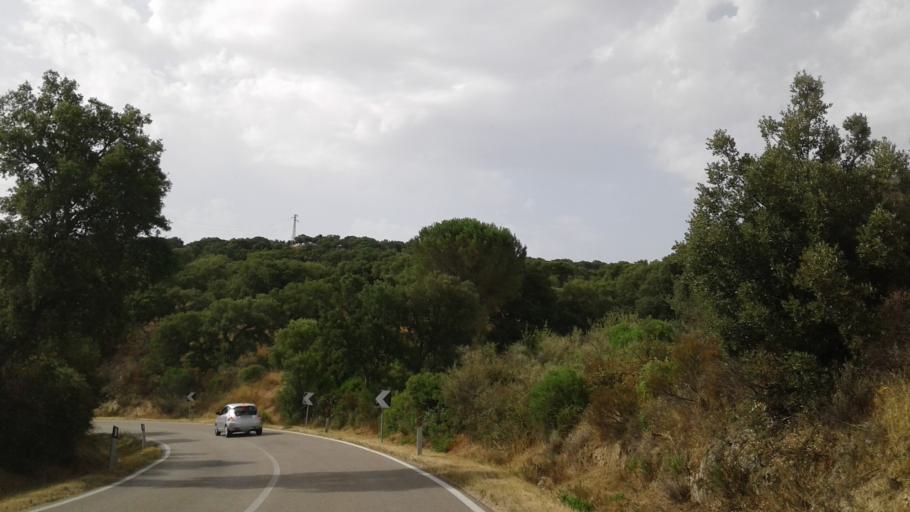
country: IT
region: Sardinia
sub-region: Provincia di Olbia-Tempio
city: Sant'Antonio di Gallura
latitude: 40.9595
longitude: 9.2947
